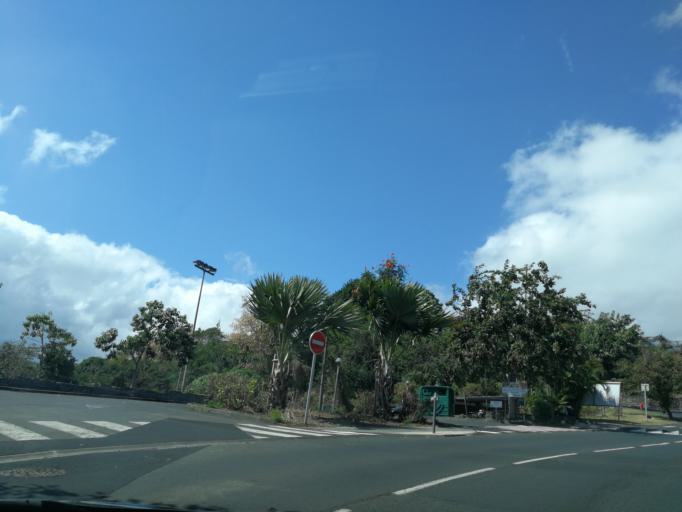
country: RE
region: Reunion
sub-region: Reunion
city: Saint-Denis
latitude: -20.9067
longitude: 55.4825
